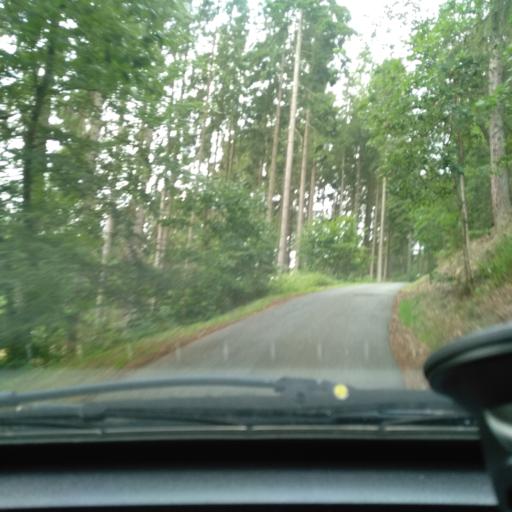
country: DE
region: Hesse
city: Dillenburg
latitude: 50.7968
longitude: 8.3167
